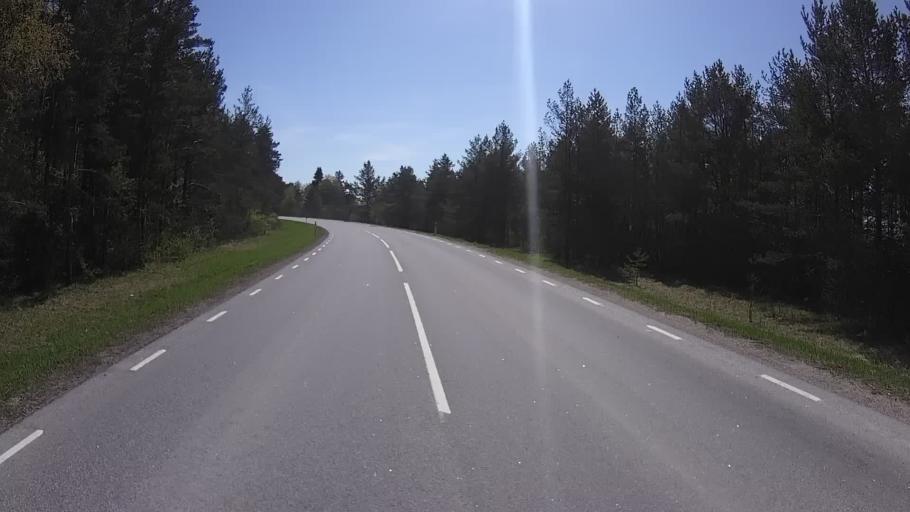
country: EE
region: Harju
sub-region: Keila linn
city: Keila
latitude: 59.3001
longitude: 24.3238
